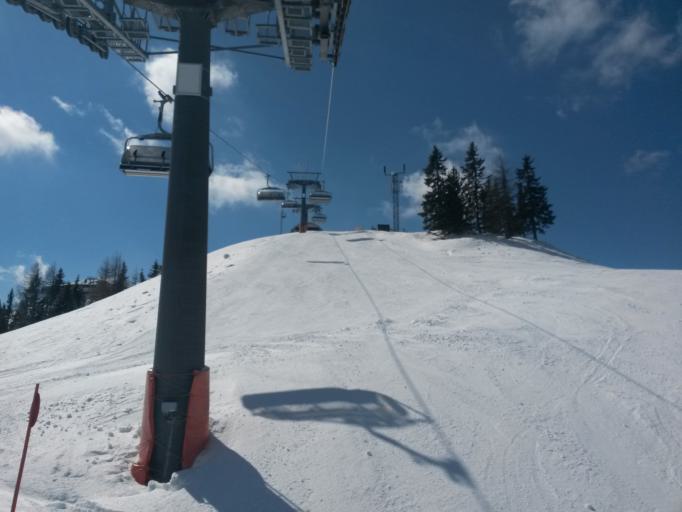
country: AT
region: Salzburg
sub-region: Politischer Bezirk Sankt Johann im Pongau
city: Dorfgastein
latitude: 47.2333
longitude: 13.1713
